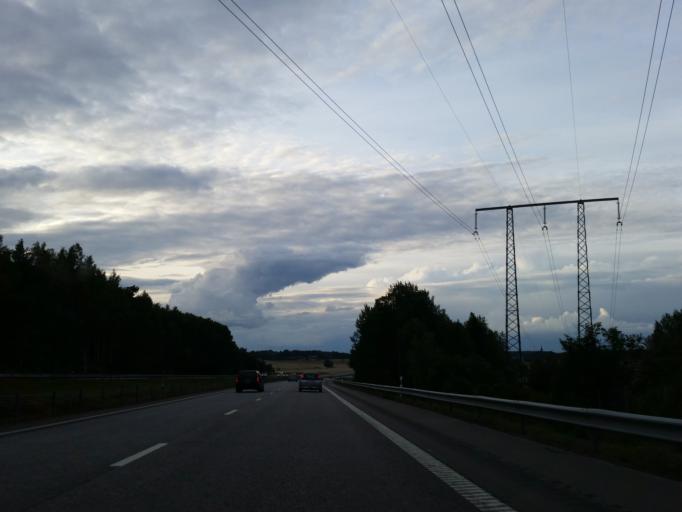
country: SE
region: Uppsala
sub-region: Uppsala Kommun
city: Alsike
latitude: 59.8026
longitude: 17.7661
